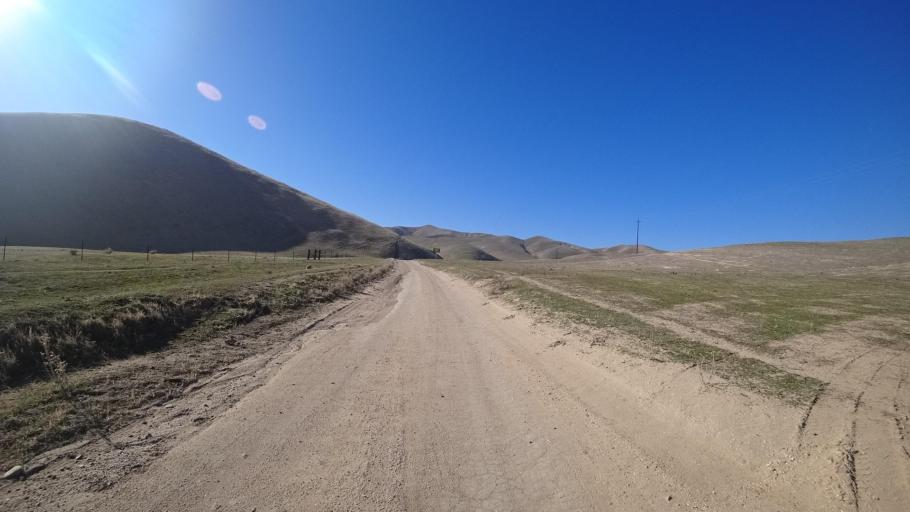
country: US
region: California
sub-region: Kern County
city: Taft Heights
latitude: 35.2296
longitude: -119.6679
